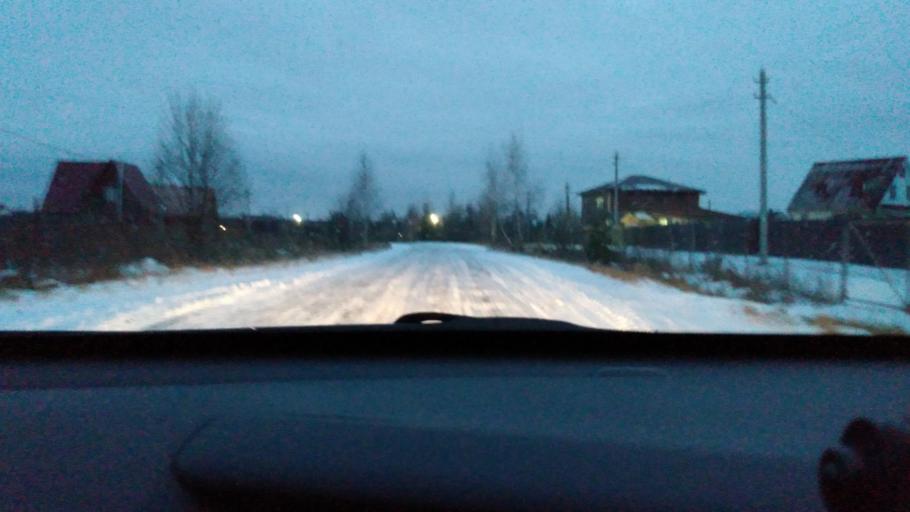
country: RU
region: Moskovskaya
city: Bronnitsy
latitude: 55.3239
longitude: 38.3463
